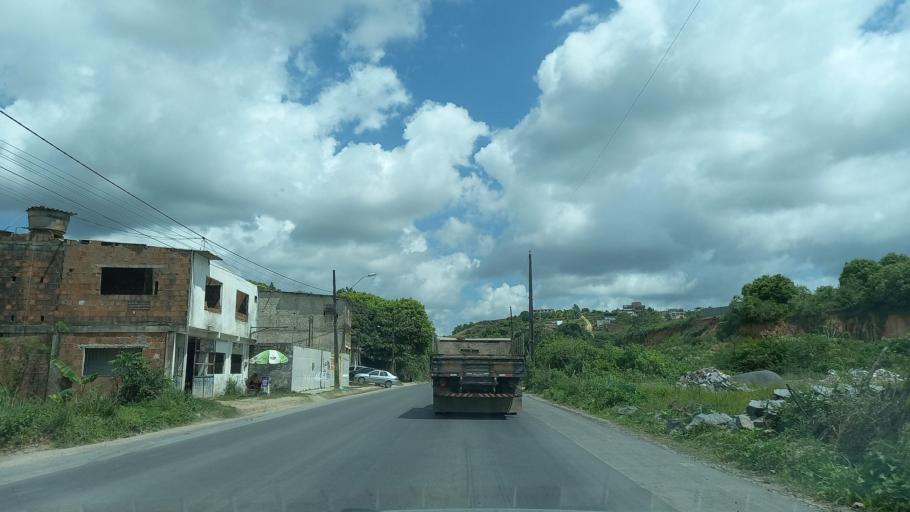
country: BR
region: Pernambuco
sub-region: Jaboatao Dos Guararapes
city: Jaboatao dos Guararapes
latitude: -8.1212
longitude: -35.0057
